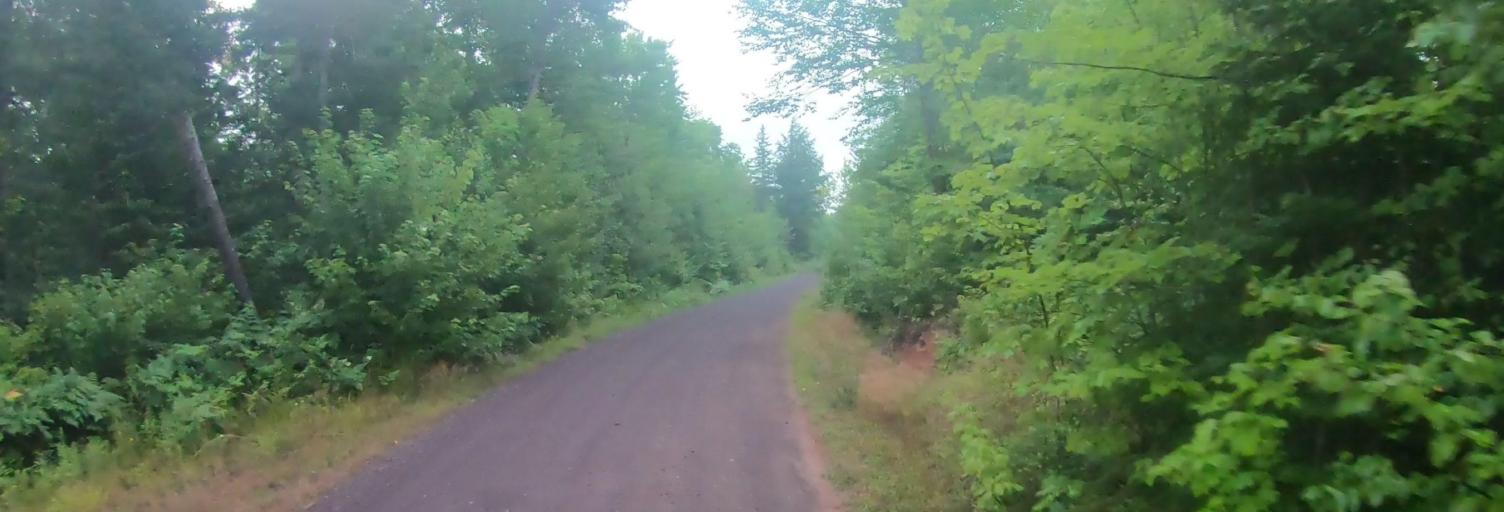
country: US
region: Michigan
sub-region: Keweenaw County
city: Eagle River
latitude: 47.2820
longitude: -88.2580
